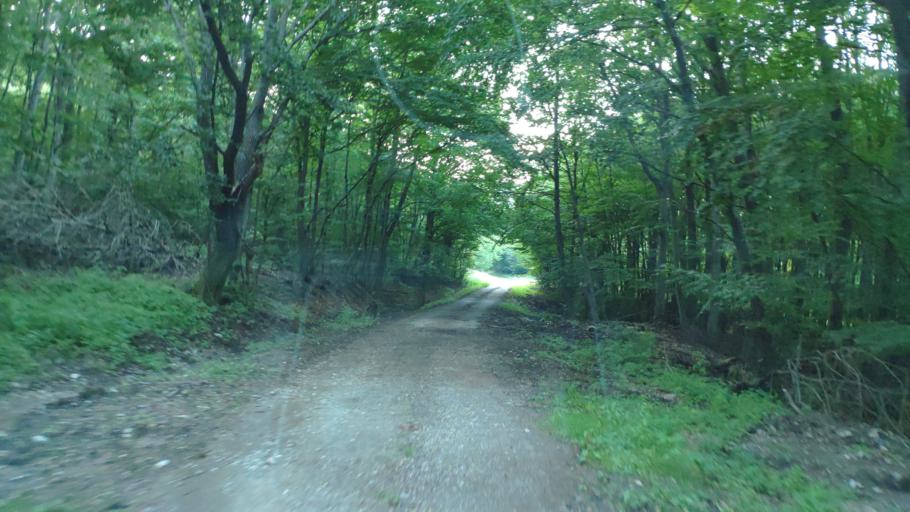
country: SK
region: Kosicky
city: Secovce
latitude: 48.5863
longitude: 21.5300
